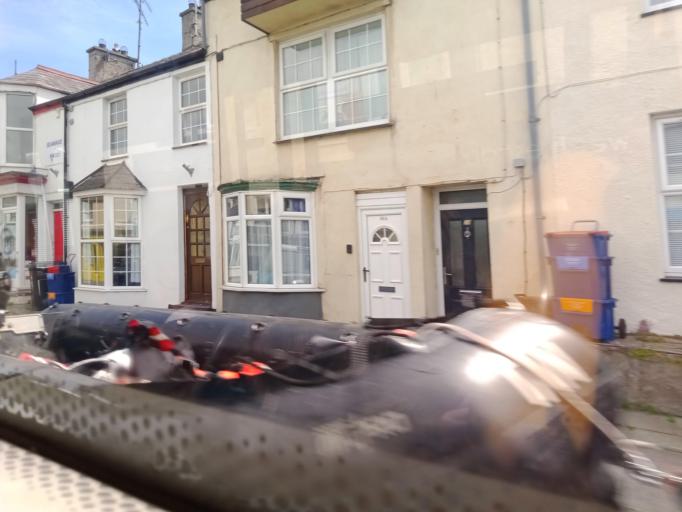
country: GB
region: Wales
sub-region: Anglesey
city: Menai Bridge
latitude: 53.2270
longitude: -4.1624
